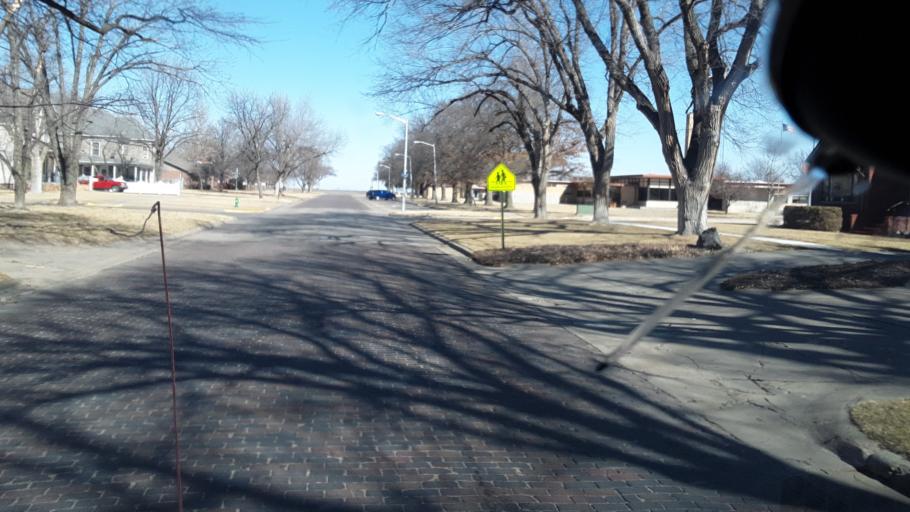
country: US
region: Kansas
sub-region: Barton County
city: Ellinwood
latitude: 38.3594
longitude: -98.5812
